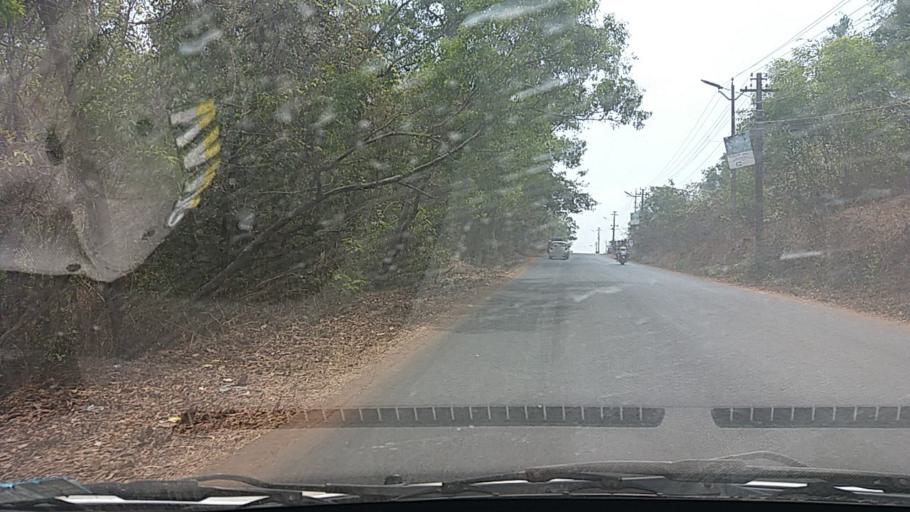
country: IN
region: Goa
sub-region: North Goa
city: Saligao
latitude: 15.5364
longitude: 73.7938
